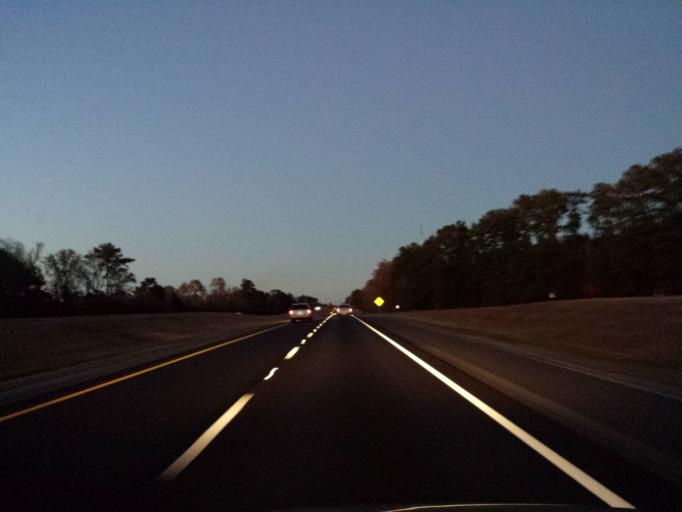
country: US
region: Mississippi
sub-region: Jones County
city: Sharon
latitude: 31.8061
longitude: -89.0533
